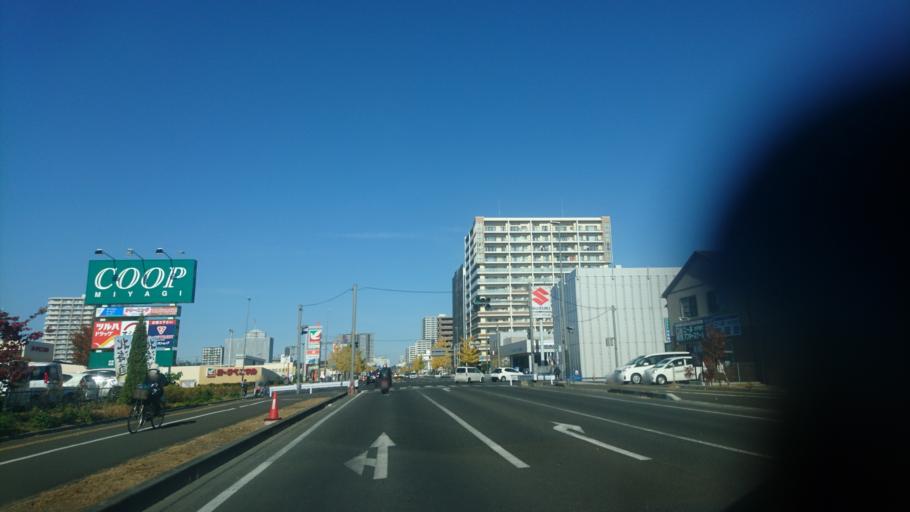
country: JP
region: Miyagi
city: Sendai
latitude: 38.2160
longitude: 140.8848
